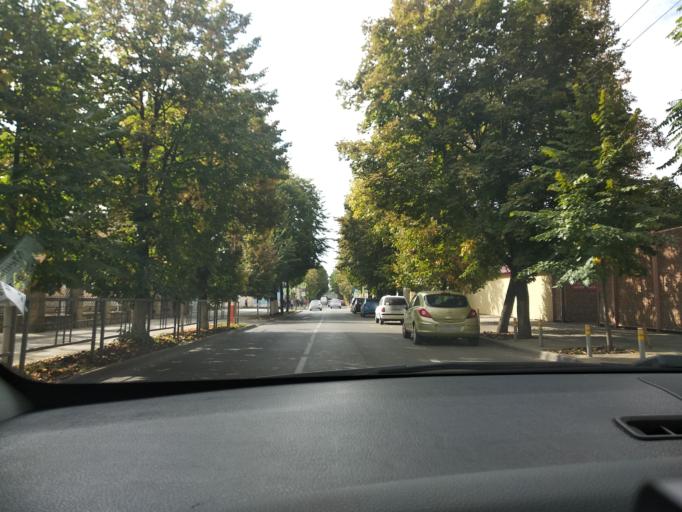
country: RU
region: Krasnodarskiy
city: Krasnodar
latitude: 45.0221
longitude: 38.9764
